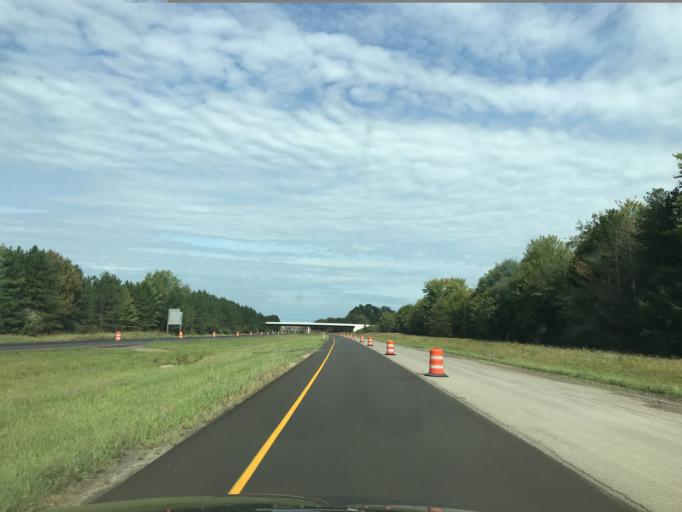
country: US
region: Ohio
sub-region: Ashtabula County
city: Jefferson
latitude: 41.7196
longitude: -80.7069
